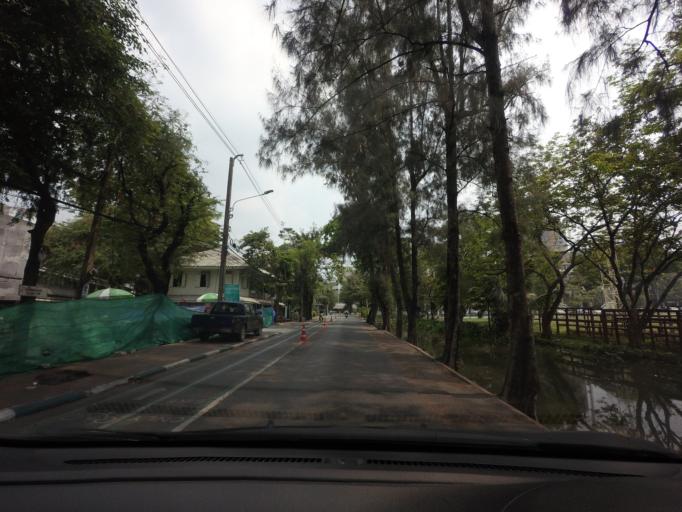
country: TH
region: Bangkok
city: Chatuchak
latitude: 13.8474
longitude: 100.5674
